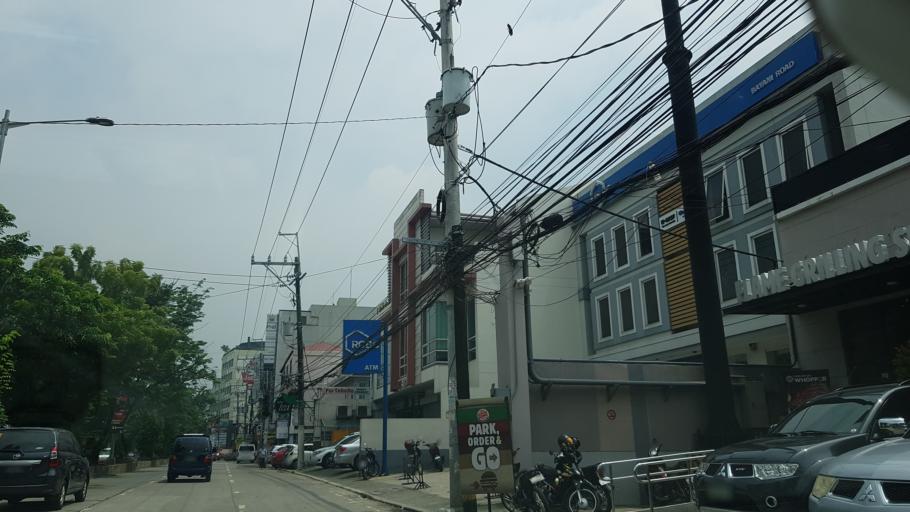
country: PH
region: Metro Manila
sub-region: Makati City
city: Makati City
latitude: 14.5278
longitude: 121.0422
